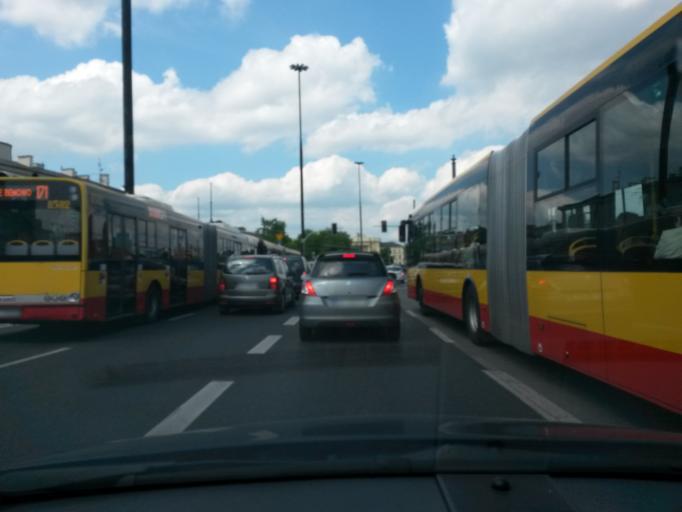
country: PL
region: Masovian Voivodeship
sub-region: Warszawa
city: Wola
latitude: 52.2436
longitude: 21.0020
